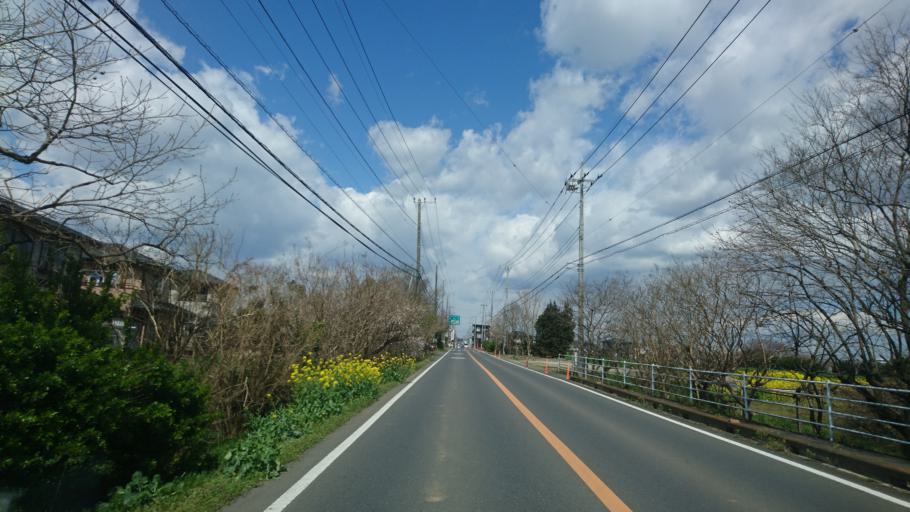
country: JP
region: Ibaraki
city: Ishige
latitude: 36.1913
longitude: 139.9555
